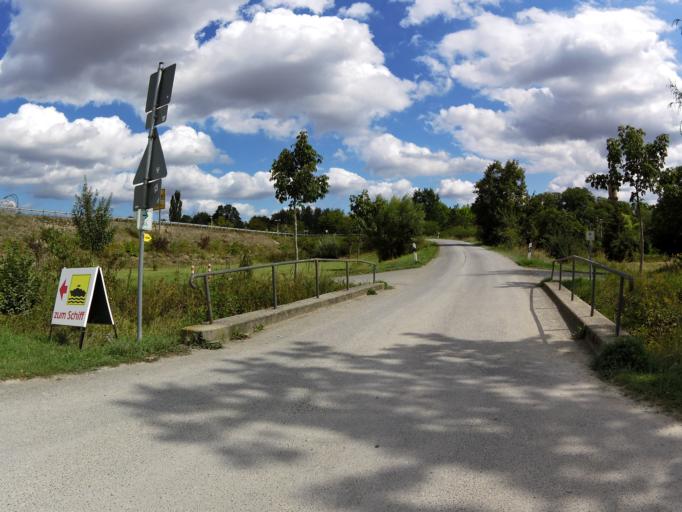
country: DE
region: Bavaria
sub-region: Regierungsbezirk Unterfranken
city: Volkach
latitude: 49.8644
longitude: 10.2215
